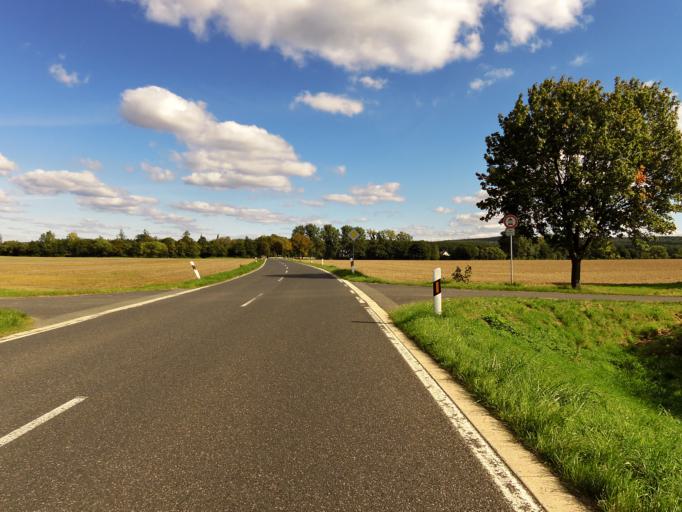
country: DE
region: North Rhine-Westphalia
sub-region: Regierungsbezirk Koln
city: Euskirchen
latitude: 50.6213
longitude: 6.8627
